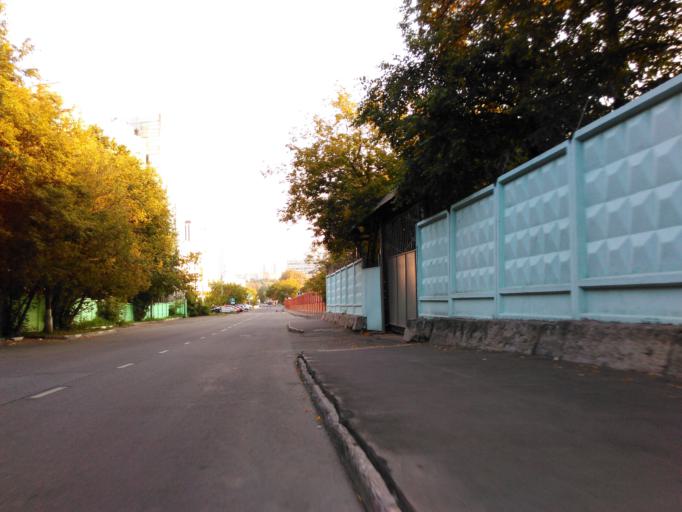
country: RU
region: Moskovskaya
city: Cheremushki
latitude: 55.6614
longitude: 37.5393
